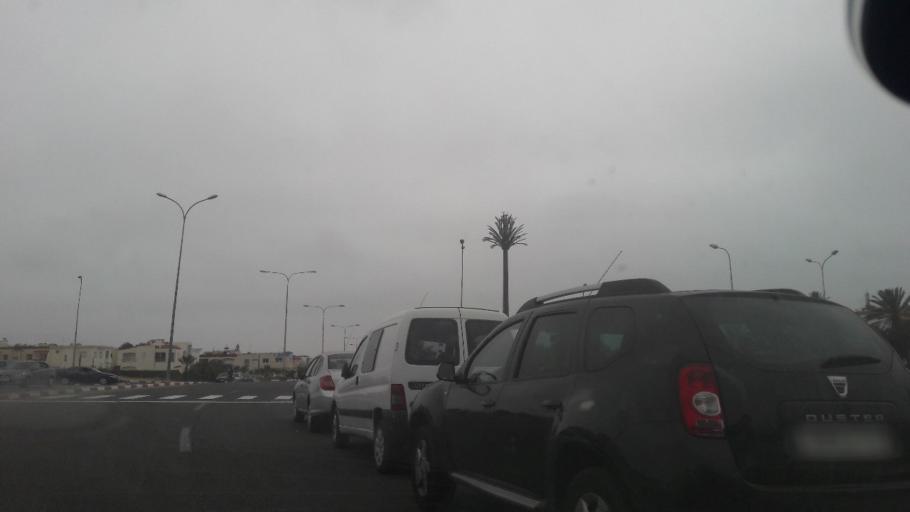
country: MA
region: Souss-Massa-Draa
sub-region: Agadir-Ida-ou-Tnan
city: Agadir
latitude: 30.3962
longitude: -9.5951
